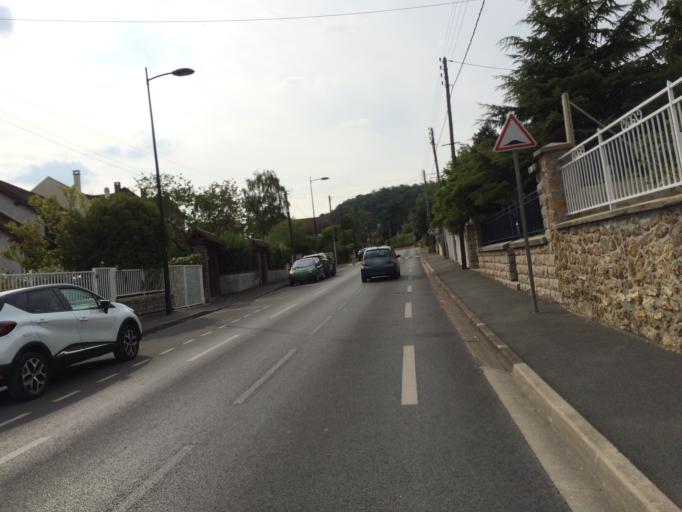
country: FR
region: Ile-de-France
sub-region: Departement de l'Essonne
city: Villebon-sur-Yvette
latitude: 48.7057
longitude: 2.2312
